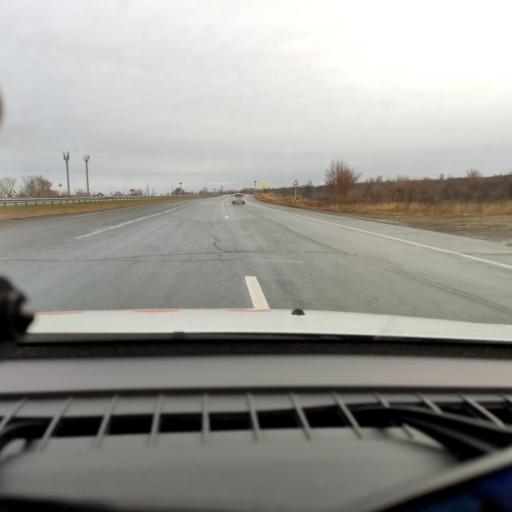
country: RU
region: Samara
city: Novokuybyshevsk
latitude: 53.0626
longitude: 50.0207
